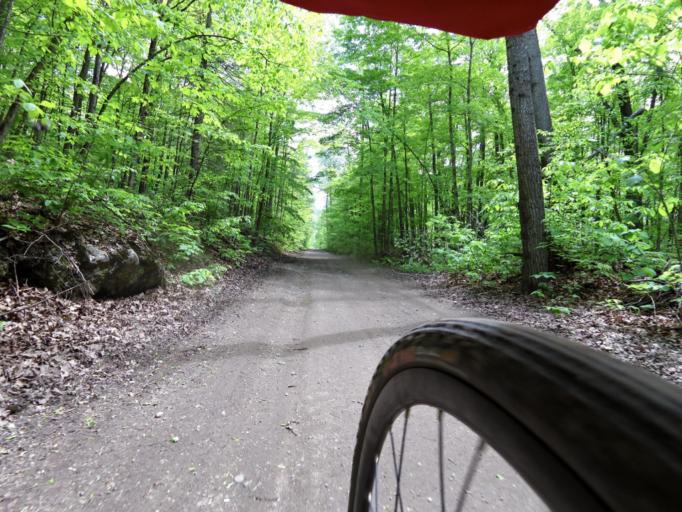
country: CA
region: Ontario
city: Renfrew
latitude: 45.1987
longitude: -76.6851
